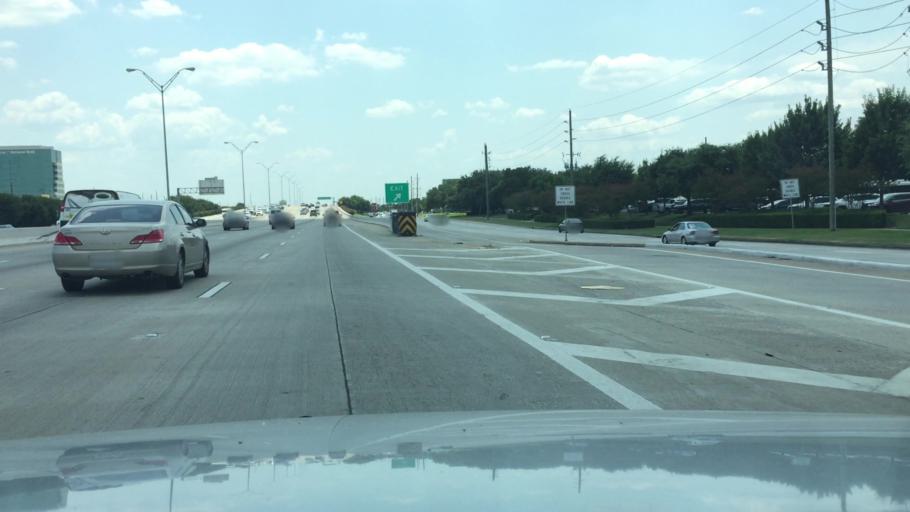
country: US
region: Texas
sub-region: Harris County
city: Bunker Hill Village
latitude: 29.7101
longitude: -95.5578
